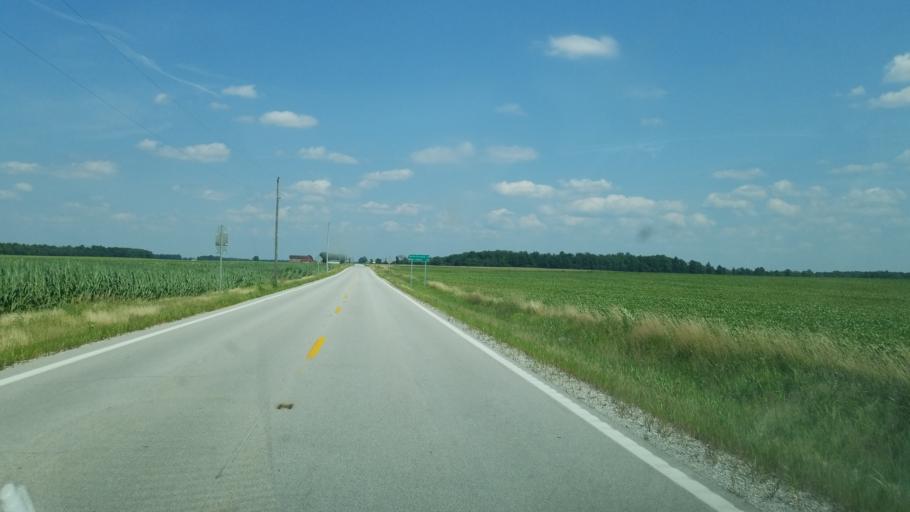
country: US
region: Ohio
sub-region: Huron County
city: Willard
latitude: 41.1243
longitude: -82.8573
